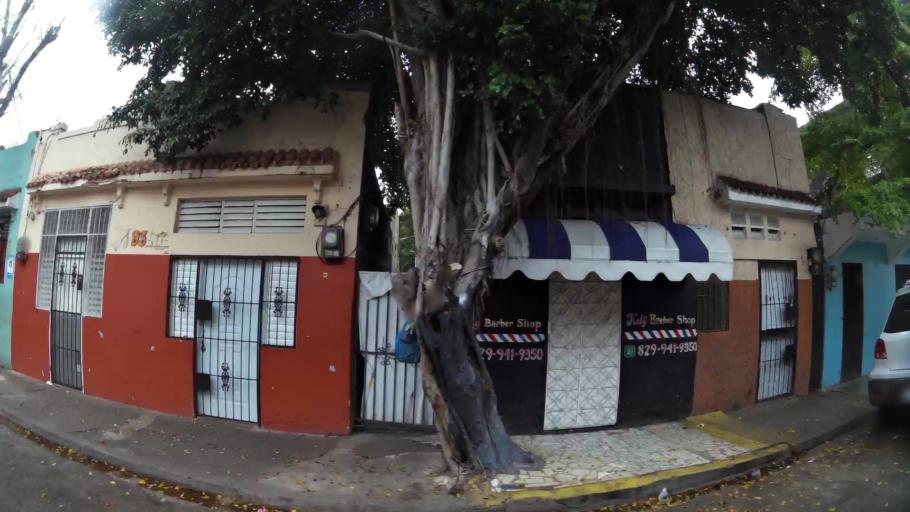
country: DO
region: Nacional
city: San Carlos
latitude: 18.4786
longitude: -69.8971
